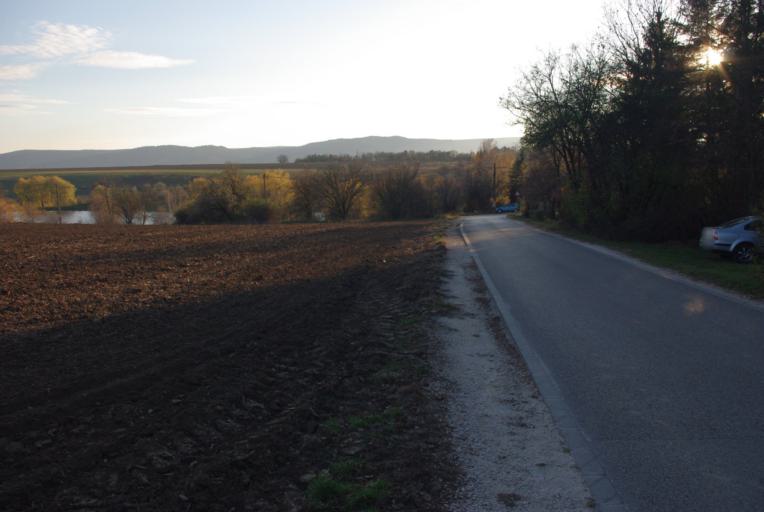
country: HU
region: Pest
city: Pilisszanto
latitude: 47.6480
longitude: 18.9113
